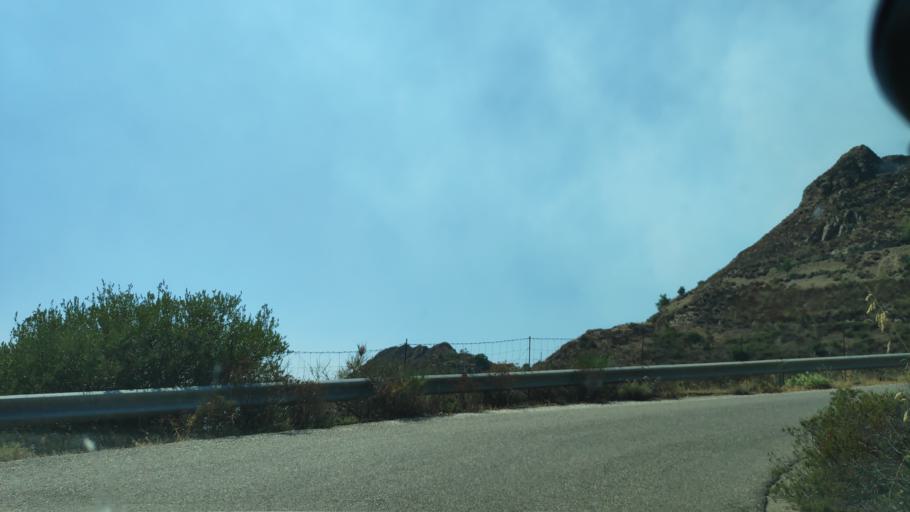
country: IT
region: Calabria
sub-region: Provincia di Reggio Calabria
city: Bova
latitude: 37.9996
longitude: 15.9282
